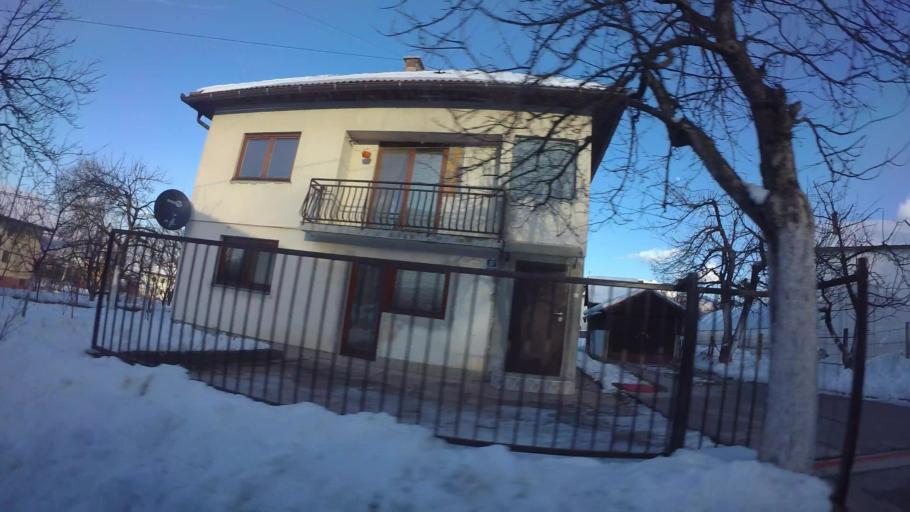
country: BA
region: Federation of Bosnia and Herzegovina
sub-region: Kanton Sarajevo
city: Sarajevo
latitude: 43.8087
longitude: 18.3553
